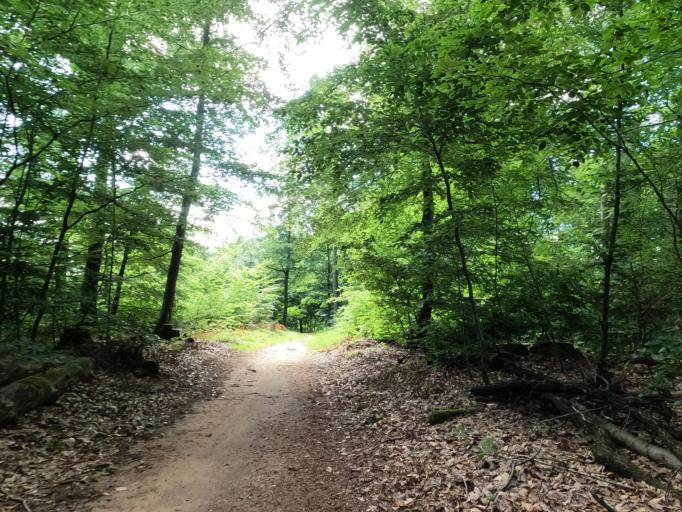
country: DE
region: Hesse
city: Niederrad
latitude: 50.0660
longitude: 8.6467
